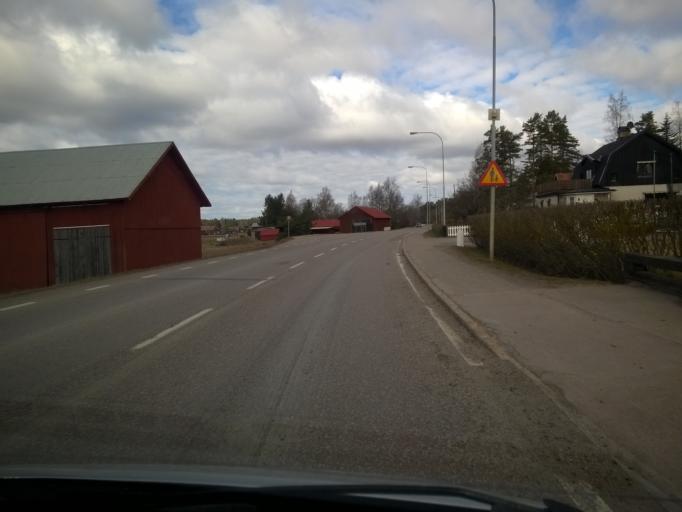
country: SE
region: Uppsala
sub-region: Tierps Kommun
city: Tierp
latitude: 60.2221
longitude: 17.4683
